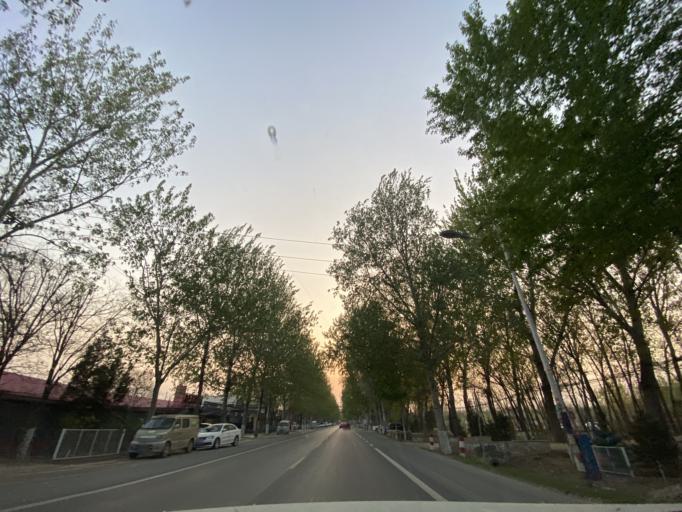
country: CN
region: Beijing
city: Weishanzhuang
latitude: 39.6146
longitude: 116.3883
